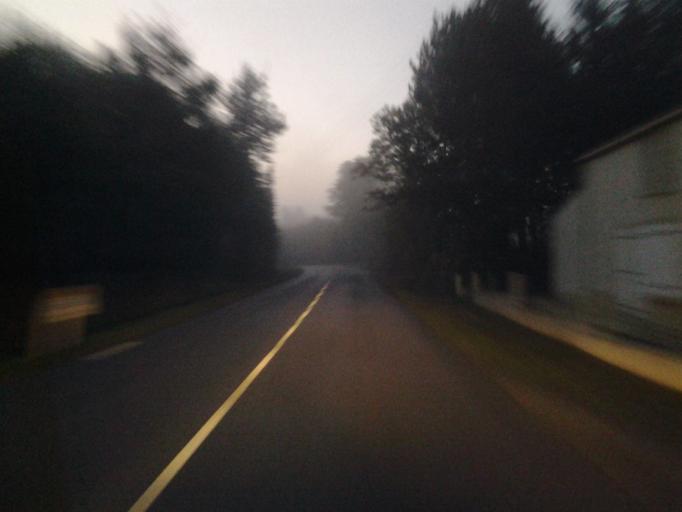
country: FR
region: Pays de la Loire
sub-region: Departement de la Vendee
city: Nesmy
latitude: 46.5830
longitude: -1.3890
